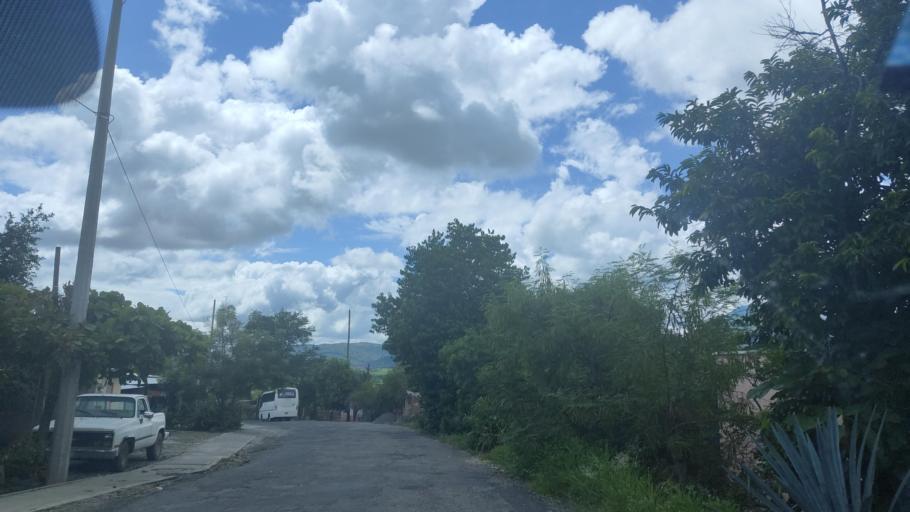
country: MX
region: Nayarit
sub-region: Ahuacatlan
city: Ahuacatlan
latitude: 21.1279
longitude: -104.6157
